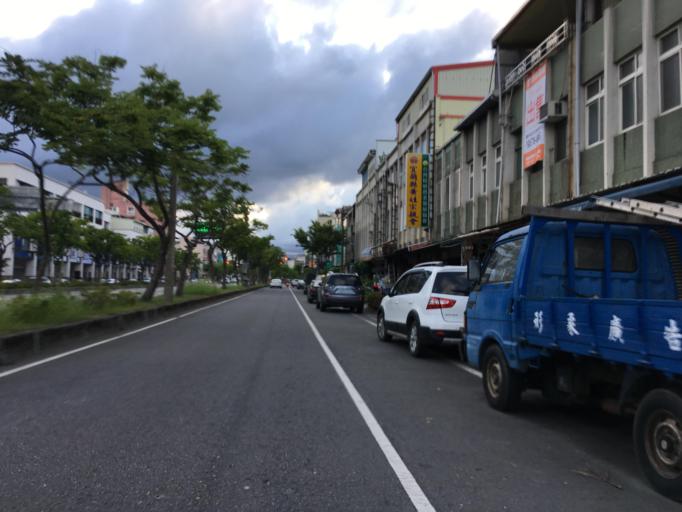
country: TW
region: Taiwan
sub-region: Yilan
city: Yilan
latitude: 24.6682
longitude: 121.7680
